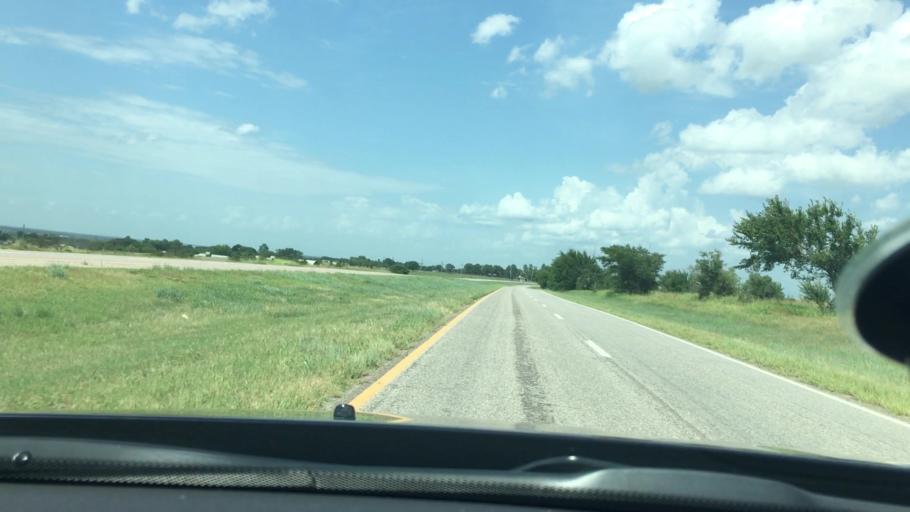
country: US
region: Oklahoma
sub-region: Pontotoc County
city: Ada
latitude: 34.7103
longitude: -96.7290
